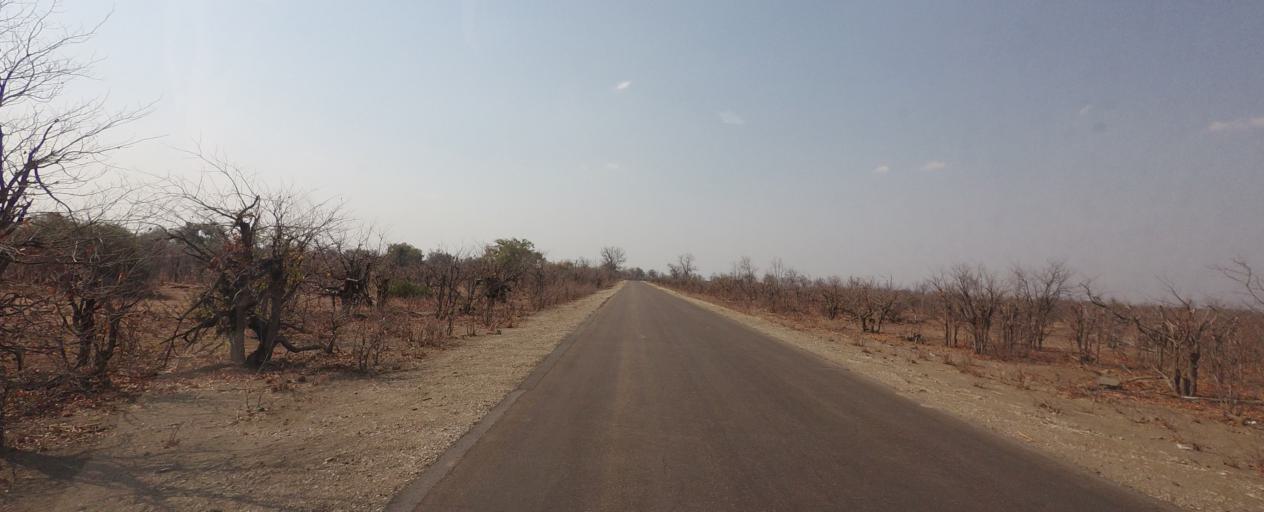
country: ZA
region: Limpopo
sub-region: Mopani District Municipality
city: Giyani
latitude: -23.1066
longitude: 31.3850
